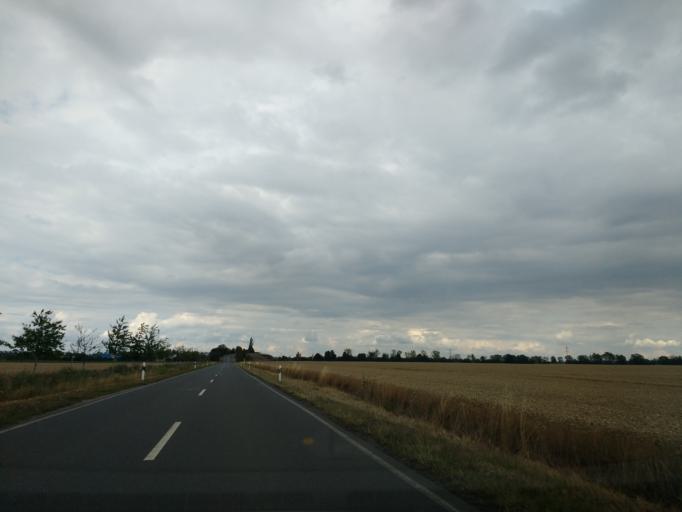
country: DE
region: Saxony-Anhalt
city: Dolbau
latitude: 51.4644
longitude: 12.0828
